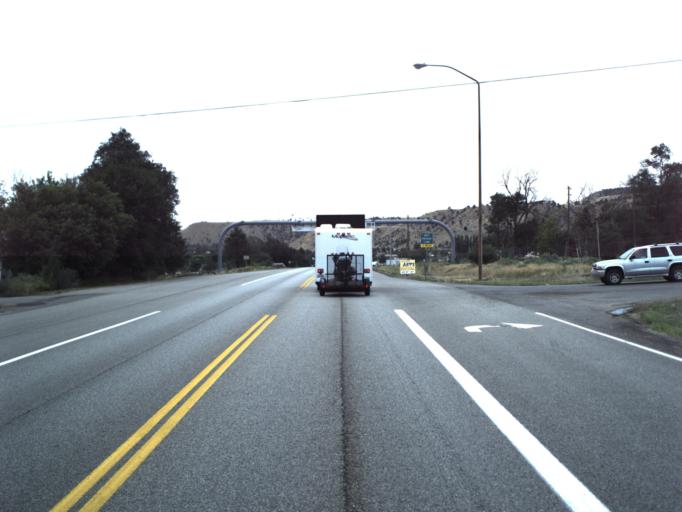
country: US
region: Utah
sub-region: Carbon County
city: Helper
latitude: 39.7024
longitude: -110.8687
